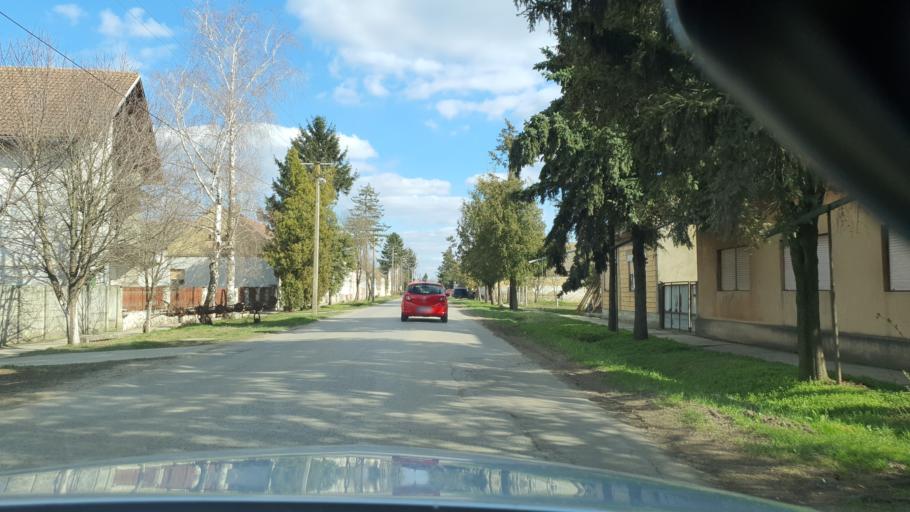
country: RS
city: Zmajevo
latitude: 45.4565
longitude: 19.6831
